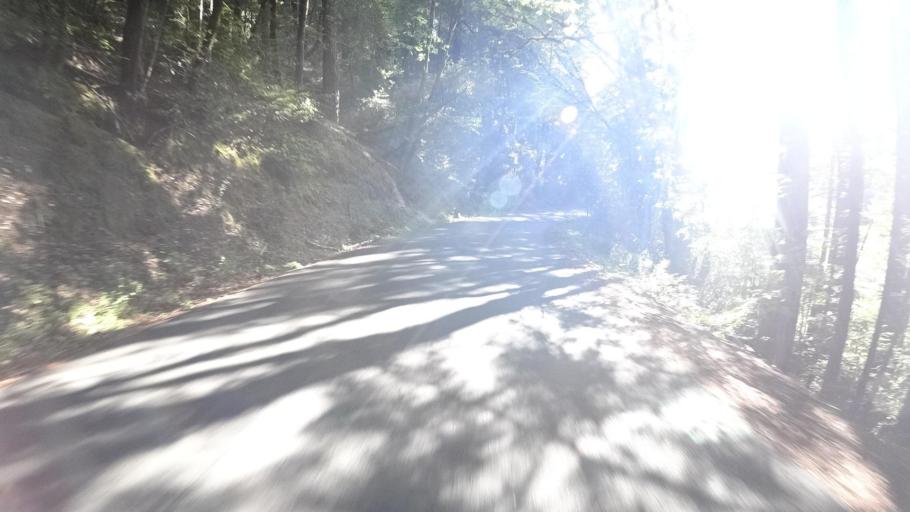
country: US
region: California
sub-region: Humboldt County
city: Rio Dell
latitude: 40.3442
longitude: -123.9383
